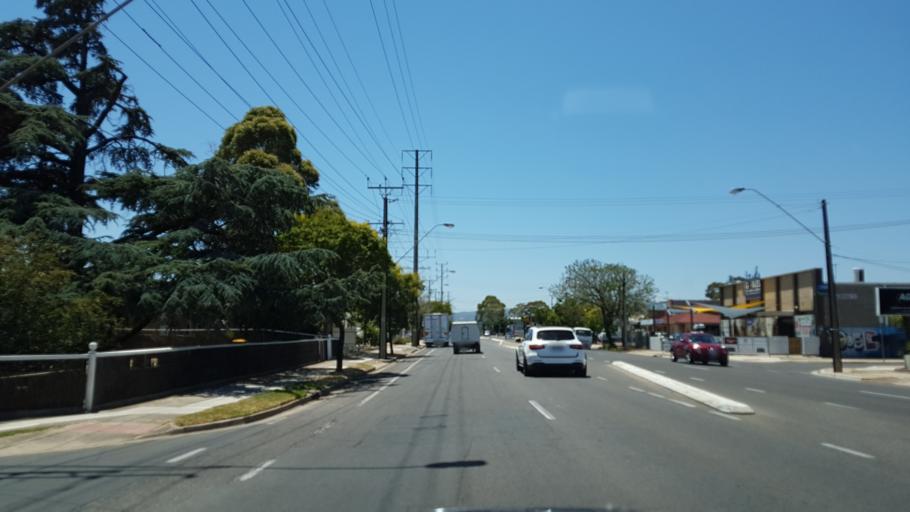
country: AU
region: South Australia
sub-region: City of West Torrens
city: Plympton
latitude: -34.9427
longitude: 138.5577
